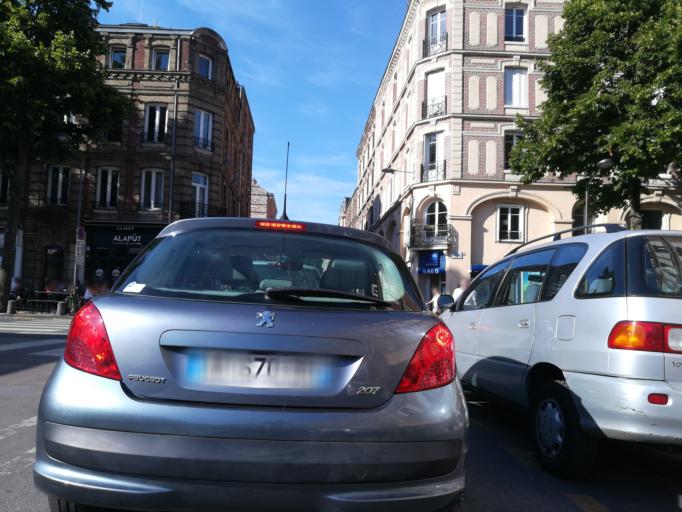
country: FR
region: Haute-Normandie
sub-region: Departement de la Seine-Maritime
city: Rouen
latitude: 49.4388
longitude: 1.1019
